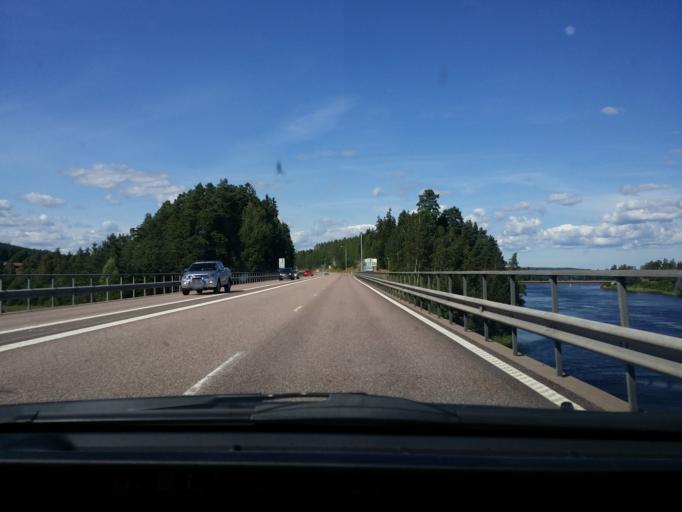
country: SE
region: Dalarna
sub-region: Hedemora Kommun
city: Brunna
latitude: 60.2395
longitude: 16.0291
